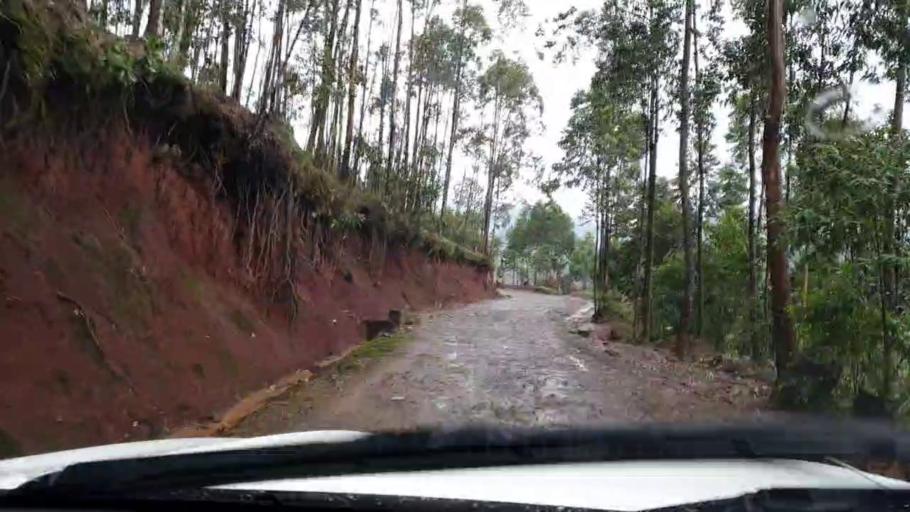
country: RW
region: Western Province
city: Cyangugu
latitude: -2.4707
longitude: 29.0322
